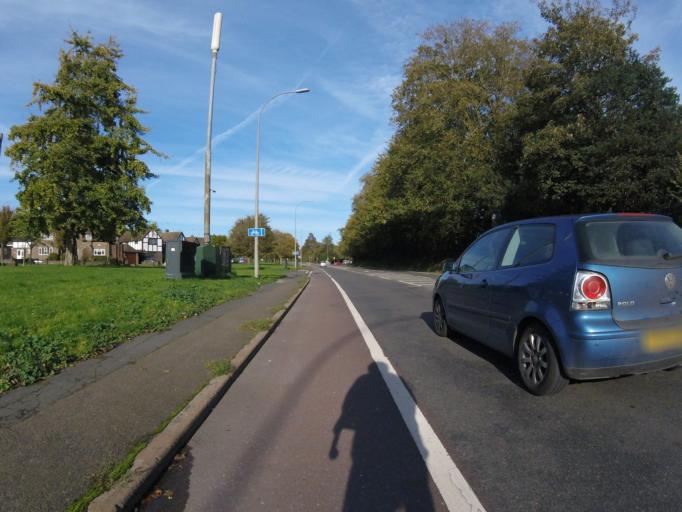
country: GB
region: England
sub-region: Brighton and Hove
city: Hove
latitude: 50.8581
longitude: -0.1528
